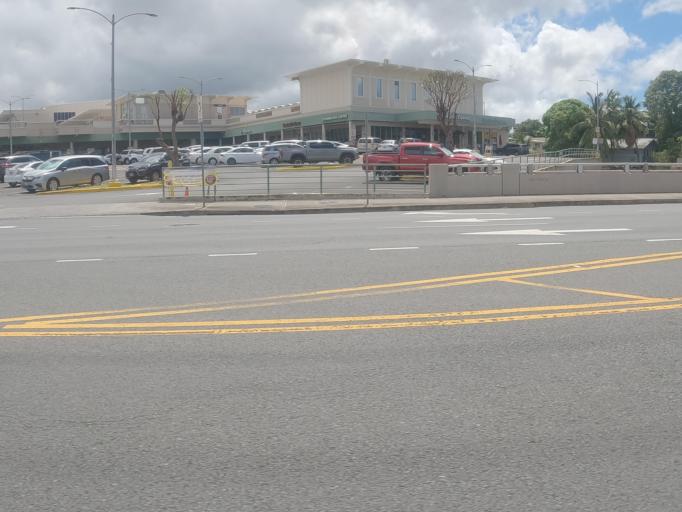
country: US
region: Hawaii
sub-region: Honolulu County
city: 'Aiea
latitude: 21.3783
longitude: -157.9310
